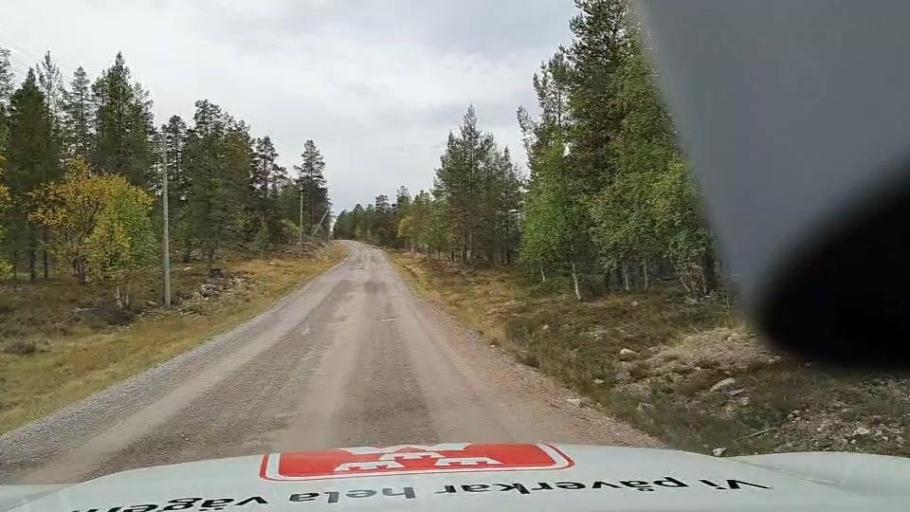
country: NO
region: Hedmark
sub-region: Engerdal
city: Engerdal
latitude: 62.0552
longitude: 12.7350
